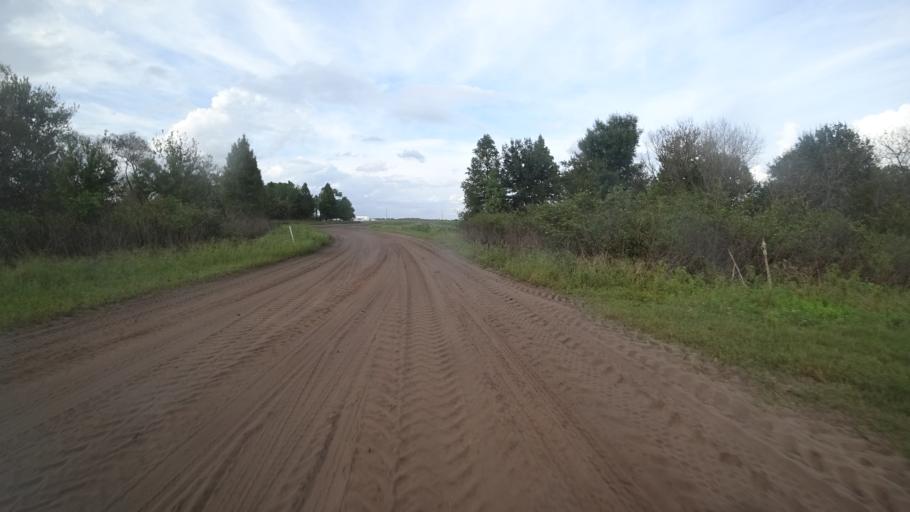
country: US
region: Florida
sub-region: Hillsborough County
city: Wimauma
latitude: 27.5808
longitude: -82.1568
